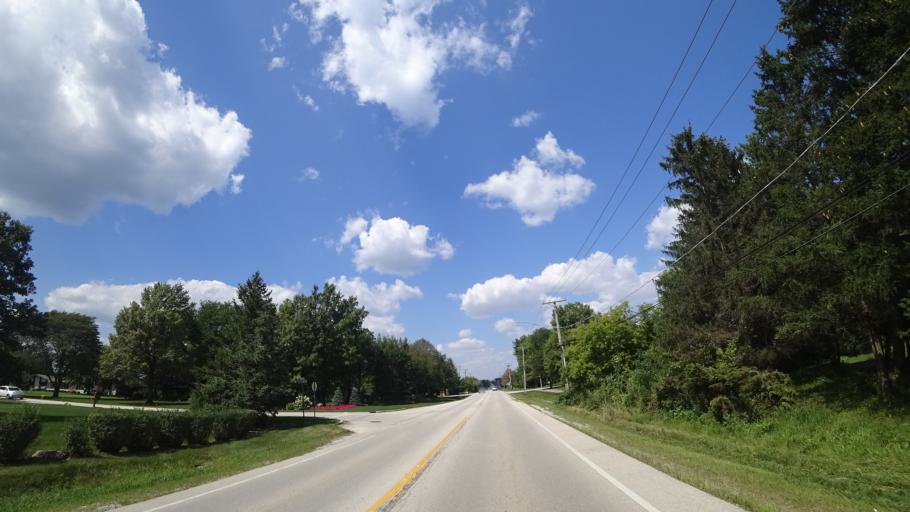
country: US
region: Illinois
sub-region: Cook County
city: Orland Park
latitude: 41.6263
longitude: -87.8195
